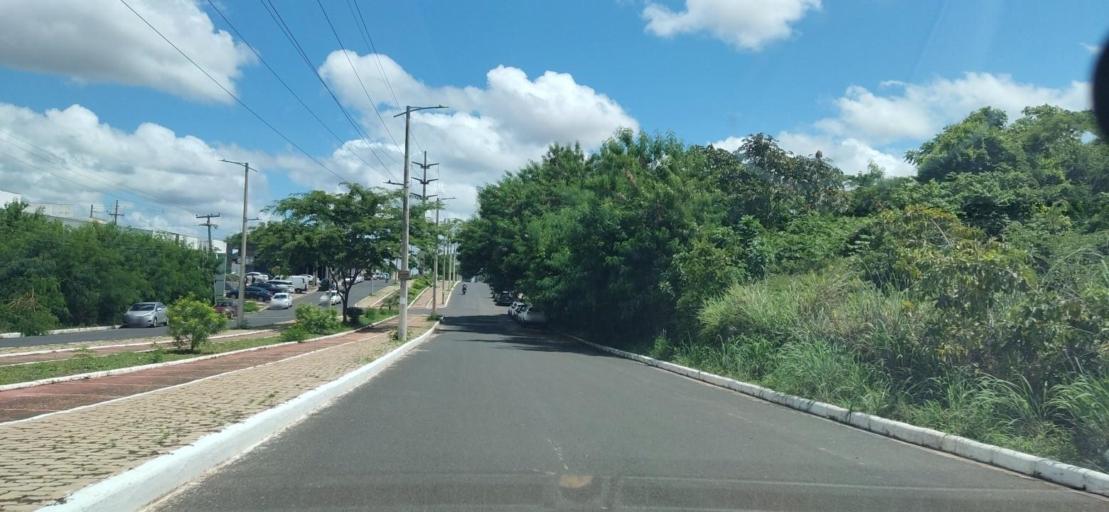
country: BR
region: Piaui
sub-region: Teresina
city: Teresina
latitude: -5.0771
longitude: -42.7514
